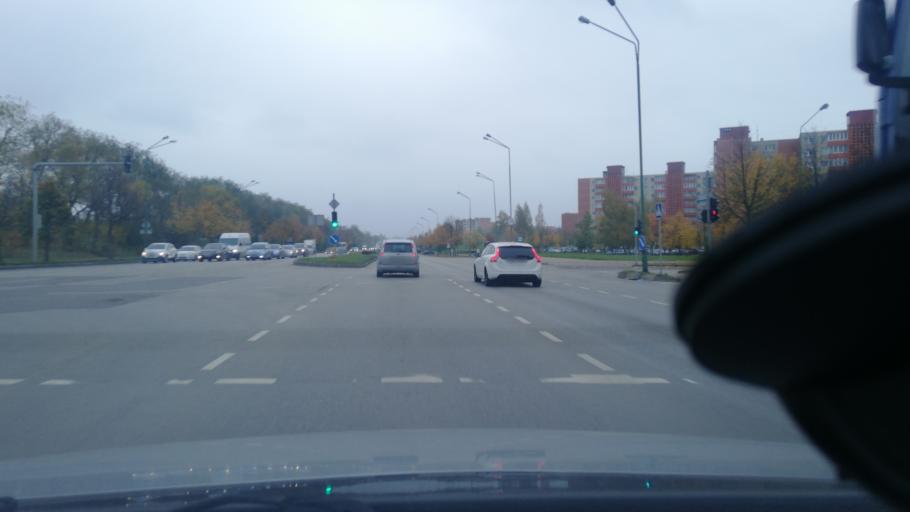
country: LT
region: Klaipedos apskritis
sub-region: Klaipeda
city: Klaipeda
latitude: 55.6755
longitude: 21.1928
